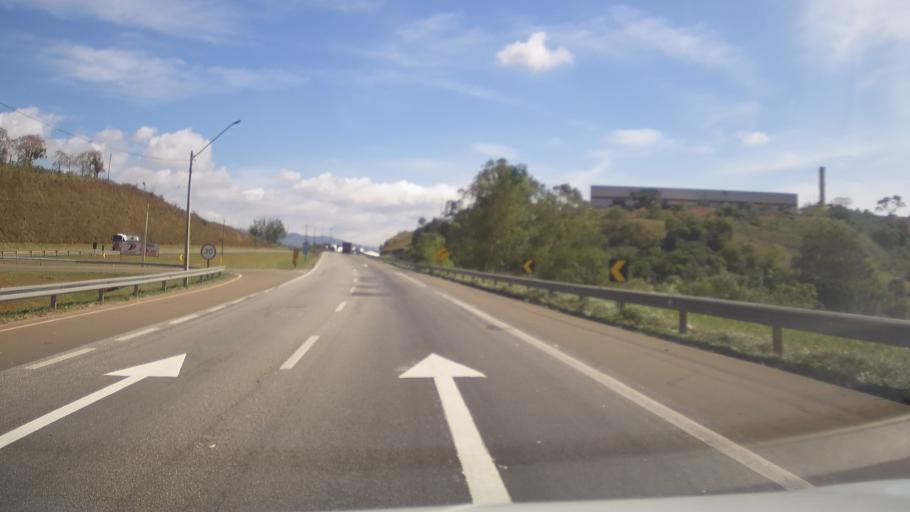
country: BR
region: Minas Gerais
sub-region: Cambui
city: Cambui
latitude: -22.5664
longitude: -46.0408
